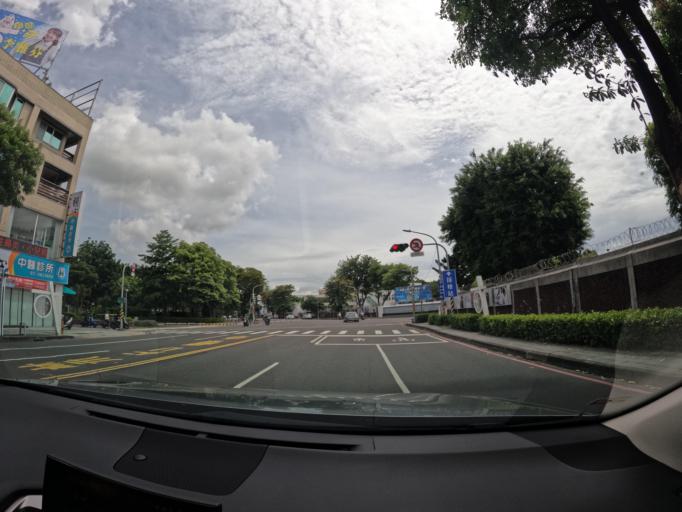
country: TW
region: Kaohsiung
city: Kaohsiung
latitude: 22.7054
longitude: 120.2927
